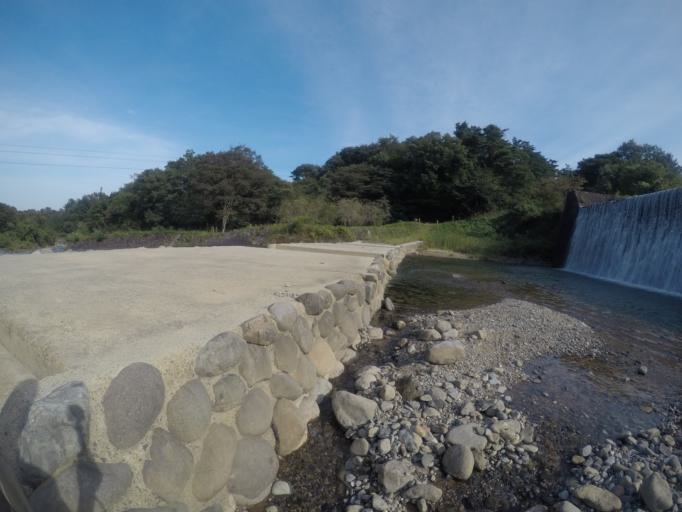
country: JP
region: Fukushima
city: Fukushima-shi
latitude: 37.7041
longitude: 140.3496
